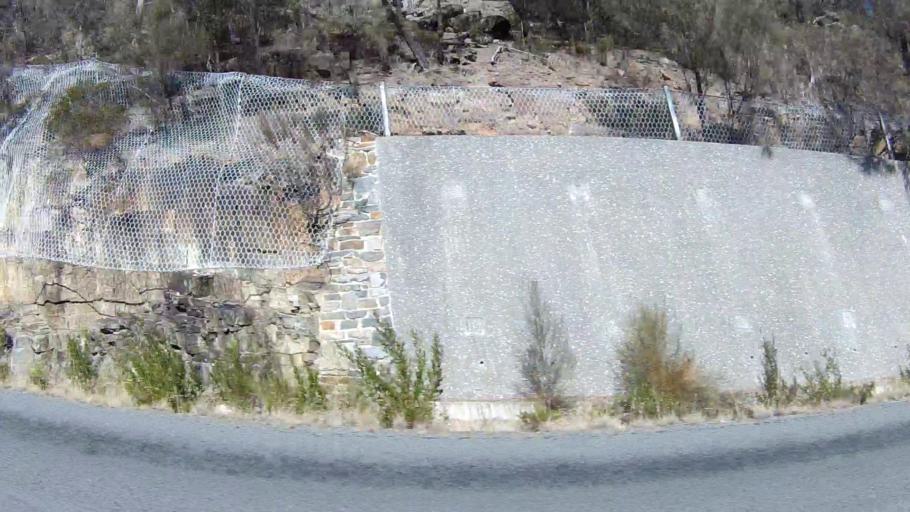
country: AU
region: Tasmania
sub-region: Sorell
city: Sorell
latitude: -42.5603
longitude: 147.8458
